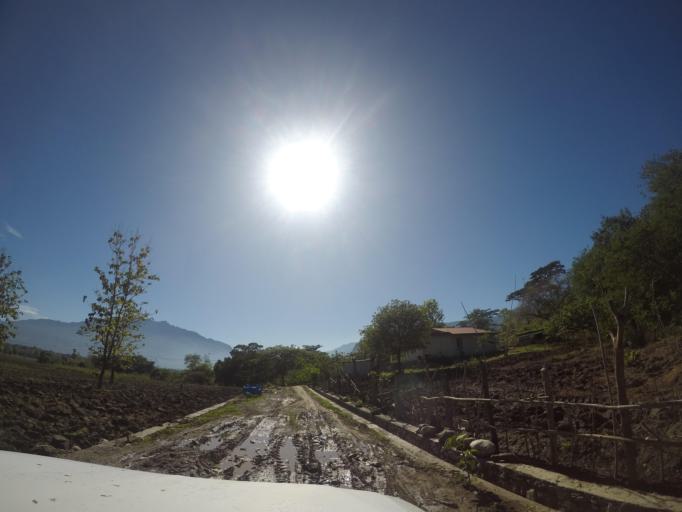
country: TL
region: Bobonaro
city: Maliana
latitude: -8.9978
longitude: 125.1908
